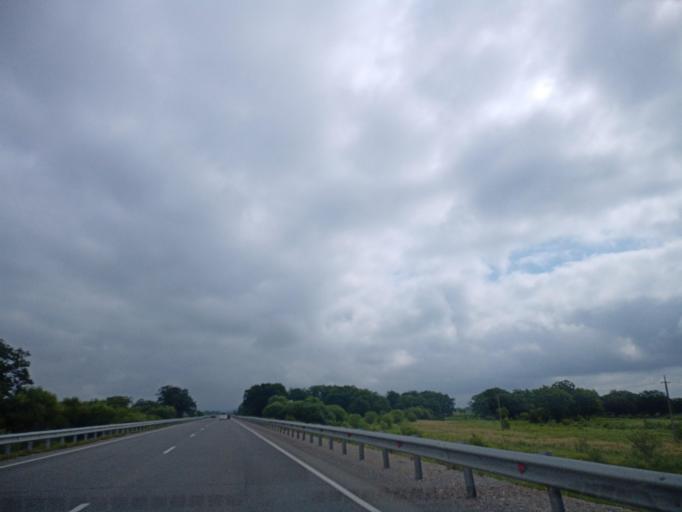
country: RU
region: Primorskiy
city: Dal'nerechensk
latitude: 45.9756
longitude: 133.7922
